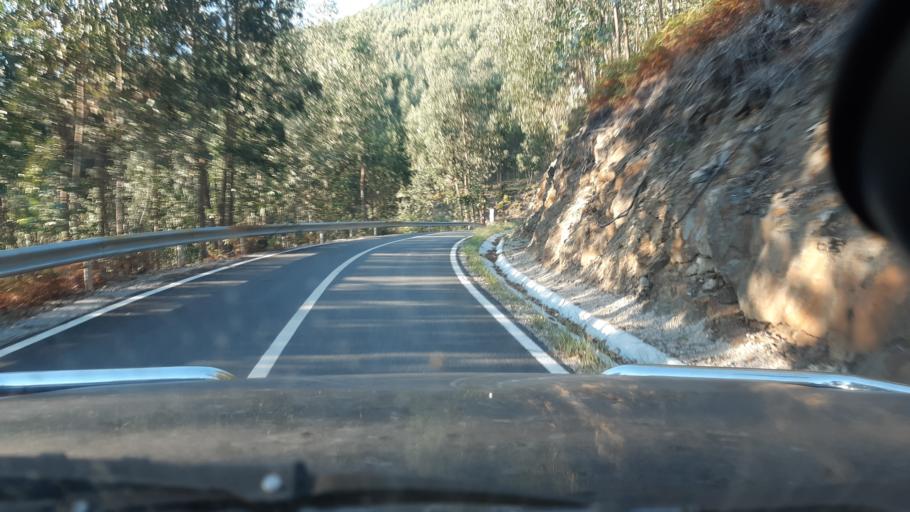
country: PT
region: Viseu
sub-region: Mortagua
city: Mortagua
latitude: 40.5366
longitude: -8.2451
